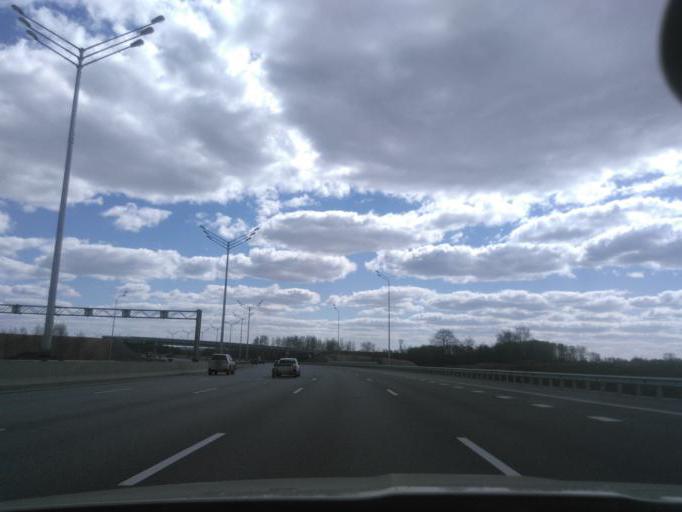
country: RU
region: Moskovskaya
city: Novopodrezkovo
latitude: 55.9543
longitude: 37.3733
